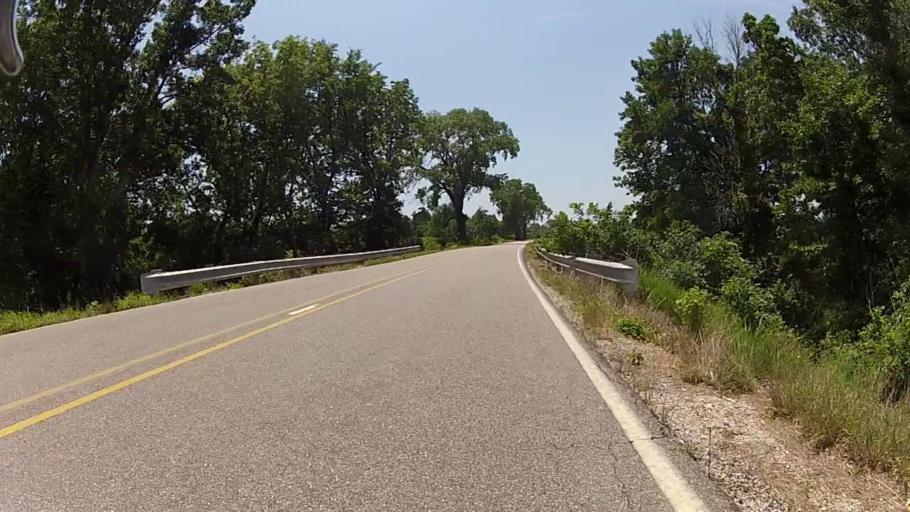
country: US
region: Kansas
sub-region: Montgomery County
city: Cherryvale
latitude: 37.2146
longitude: -95.5386
